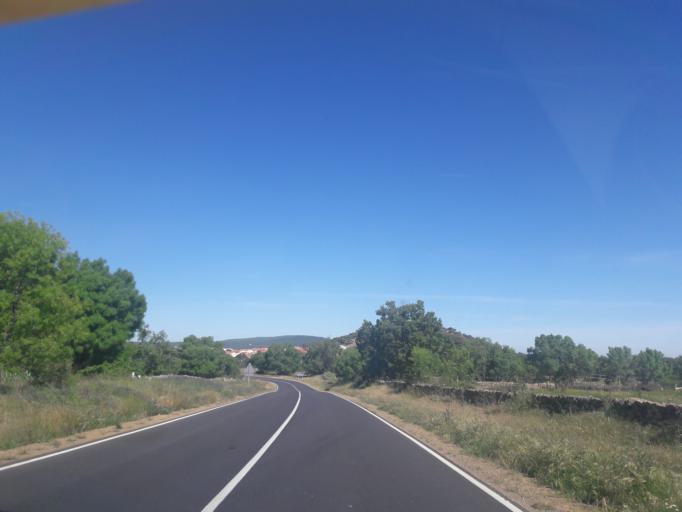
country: ES
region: Castille and Leon
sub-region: Provincia de Salamanca
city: Nava de Bejar
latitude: 40.4922
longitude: -5.6570
